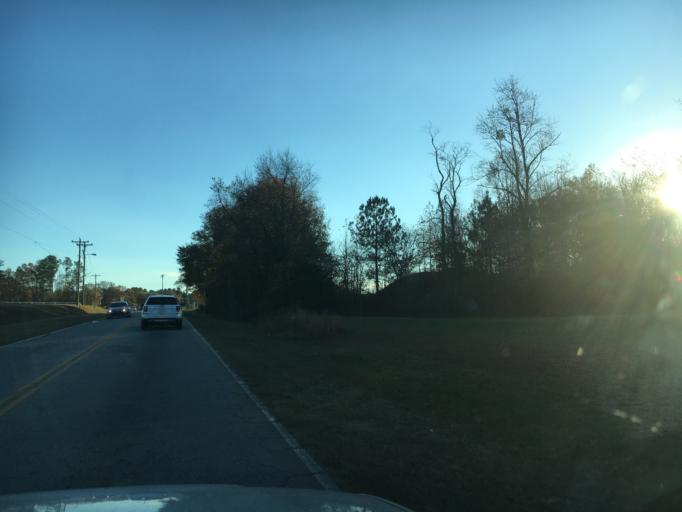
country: US
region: South Carolina
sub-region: Spartanburg County
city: Lyman
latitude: 34.9380
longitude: -82.1240
